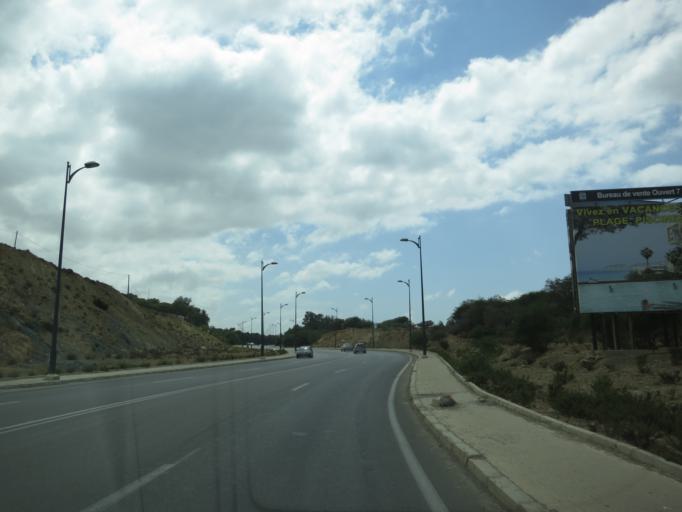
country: MA
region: Tanger-Tetouan
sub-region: Tanger-Assilah
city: Tangier
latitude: 35.8002
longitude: -5.7443
